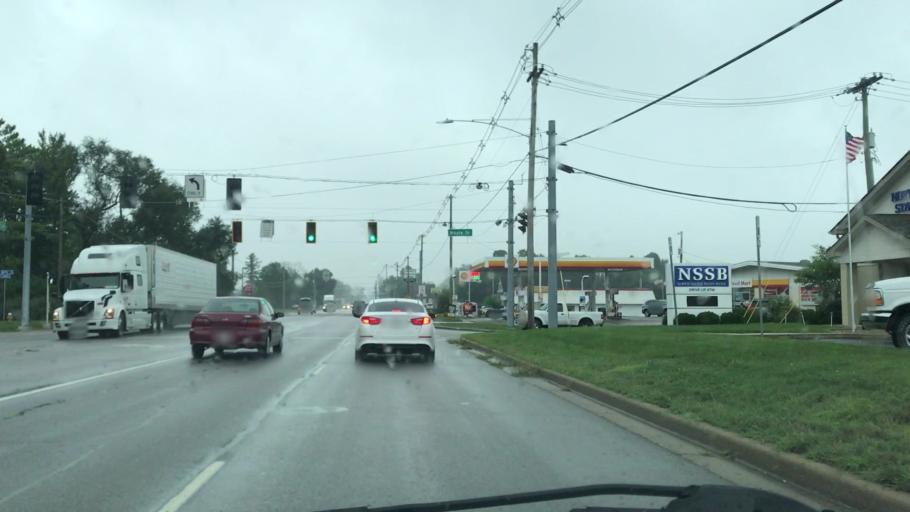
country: US
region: Indiana
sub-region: Boone County
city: Lebanon
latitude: 40.0660
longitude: -86.4729
